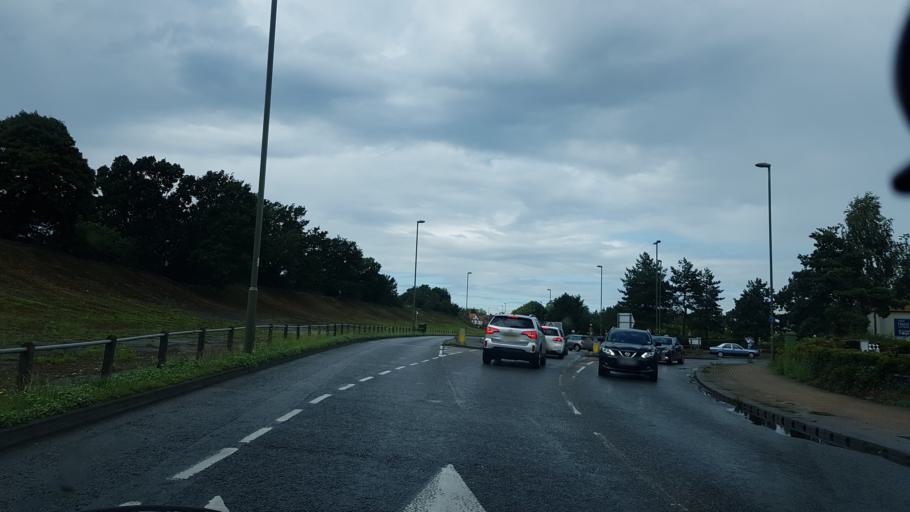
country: GB
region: England
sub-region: Surrey
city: Byfleet
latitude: 51.3434
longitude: -0.4749
